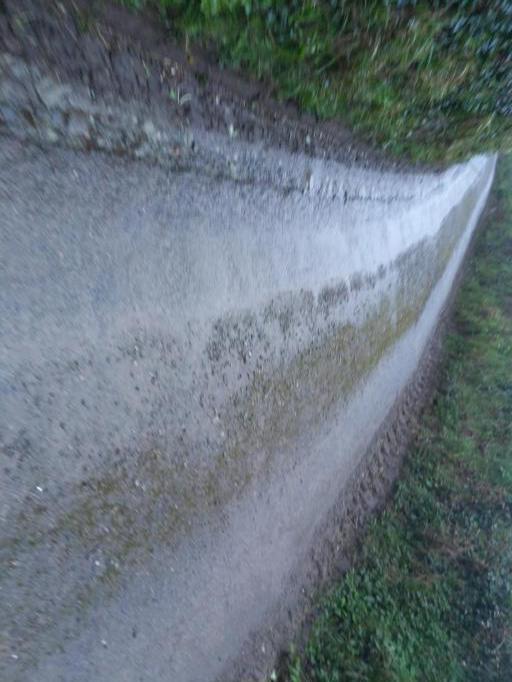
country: GB
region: England
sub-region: Cornwall
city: Torpoint
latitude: 50.3387
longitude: -4.2187
